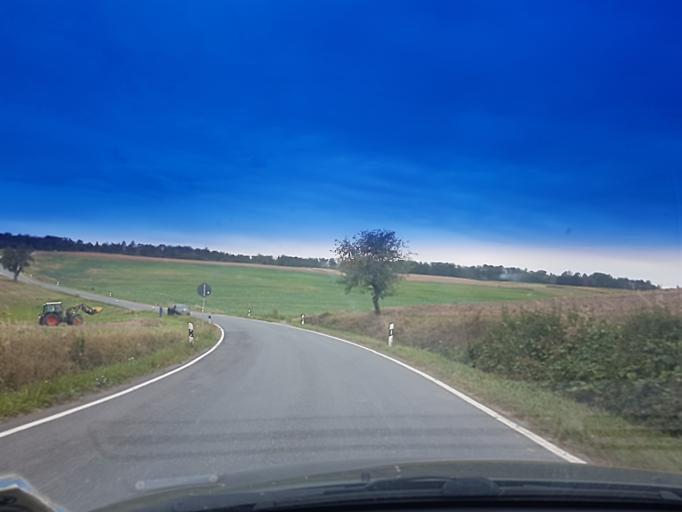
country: DE
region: Bavaria
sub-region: Regierungsbezirk Unterfranken
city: Geiselwind
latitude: 49.8177
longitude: 10.4849
